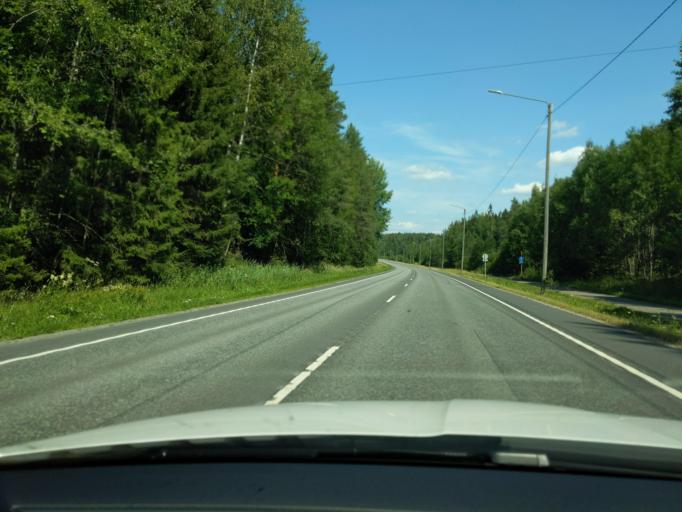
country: FI
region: Uusimaa
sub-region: Helsinki
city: Kerava
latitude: 60.3659
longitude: 25.1293
